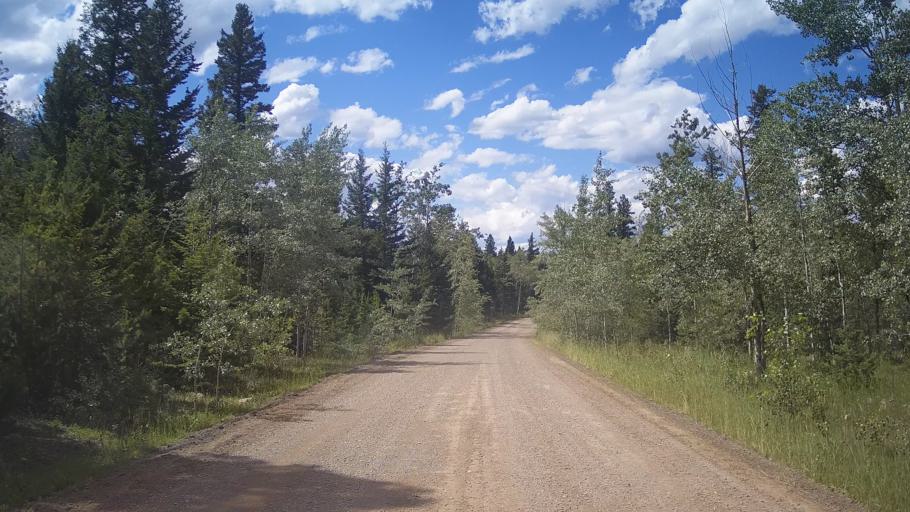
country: CA
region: British Columbia
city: Lillooet
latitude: 51.3287
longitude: -121.8891
